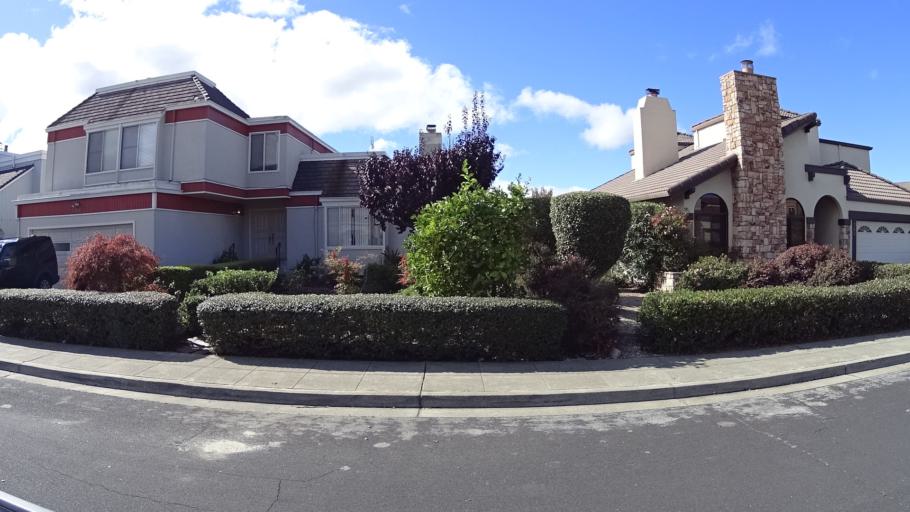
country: US
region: California
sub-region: San Mateo County
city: Foster City
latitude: 37.5618
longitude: -122.2557
